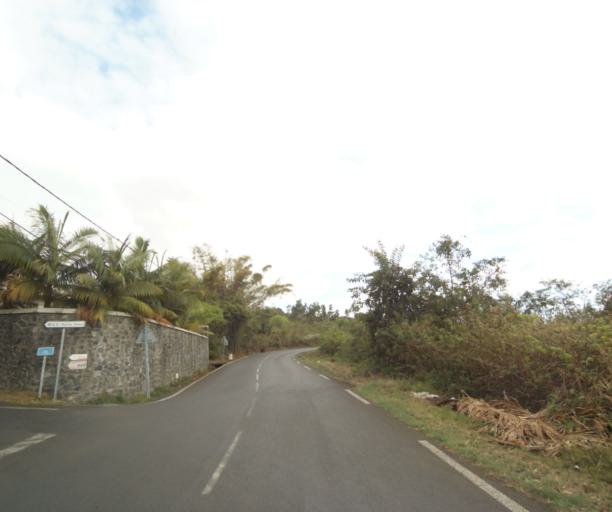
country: RE
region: Reunion
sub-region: Reunion
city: Trois-Bassins
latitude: -21.0565
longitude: 55.2828
